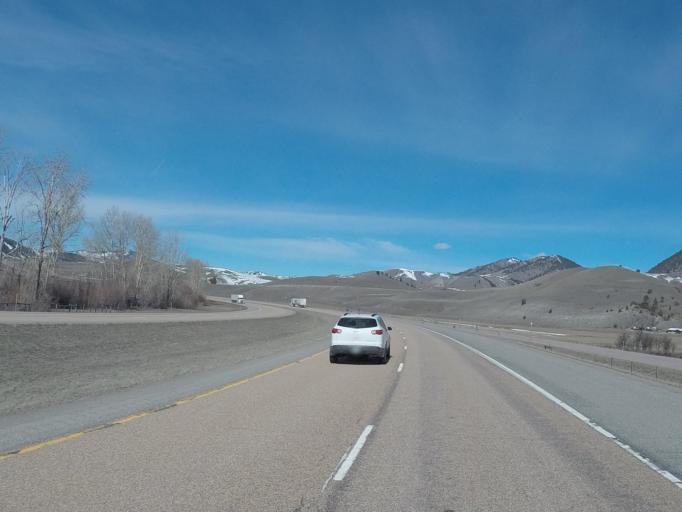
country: US
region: Montana
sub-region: Granite County
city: Philipsburg
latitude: 46.6958
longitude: -113.2063
